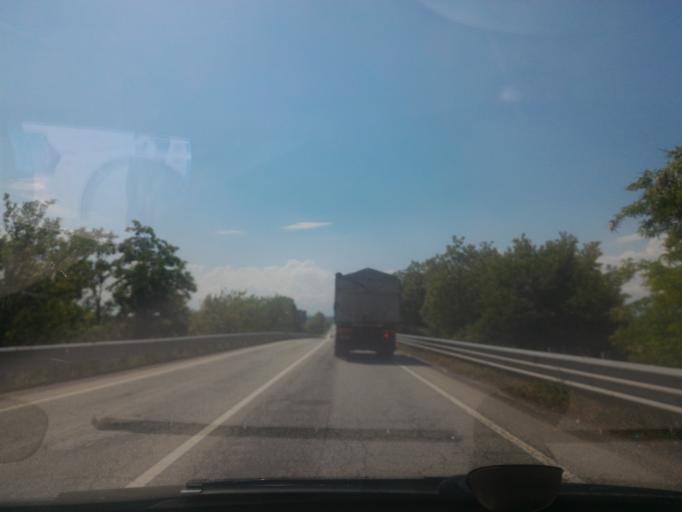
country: IT
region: Piedmont
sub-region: Provincia di Torino
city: Villastellone
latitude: 44.9219
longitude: 7.7296
